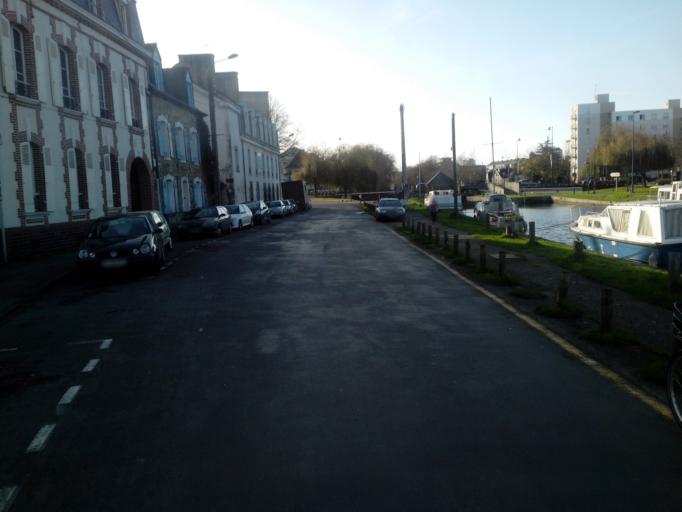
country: FR
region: Brittany
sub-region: Departement d'Ille-et-Vilaine
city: Rennes
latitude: 48.1217
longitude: -1.6808
